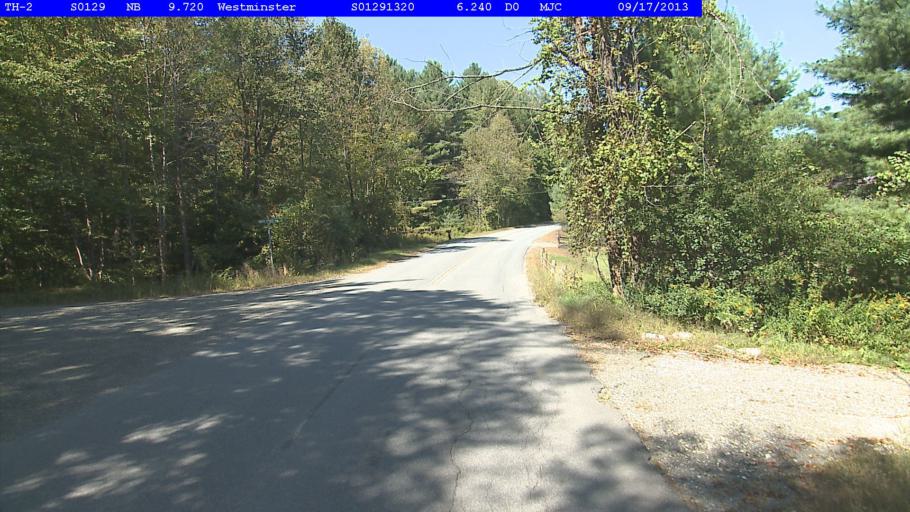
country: US
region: Vermont
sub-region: Windham County
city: Rockingham
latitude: 43.1044
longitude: -72.5378
